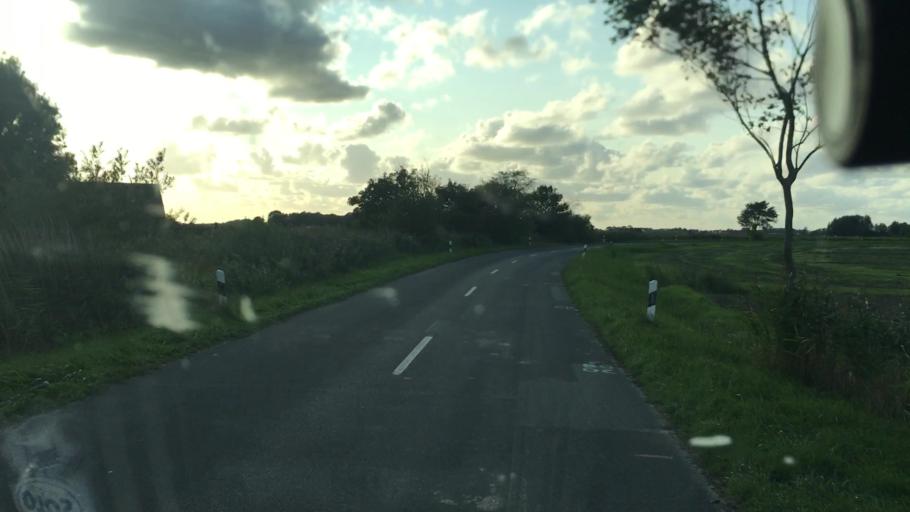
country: DE
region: Lower Saxony
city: Werdum
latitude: 53.6687
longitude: 7.7266
